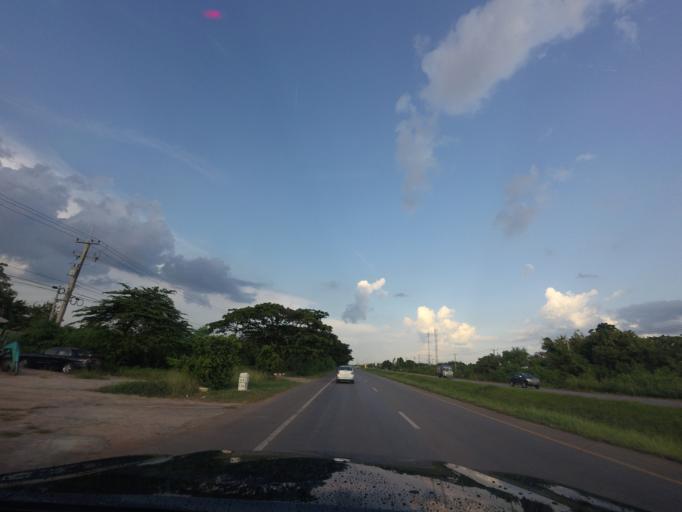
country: TH
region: Khon Kaen
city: Khon Kaen
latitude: 16.3944
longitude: 102.8529
